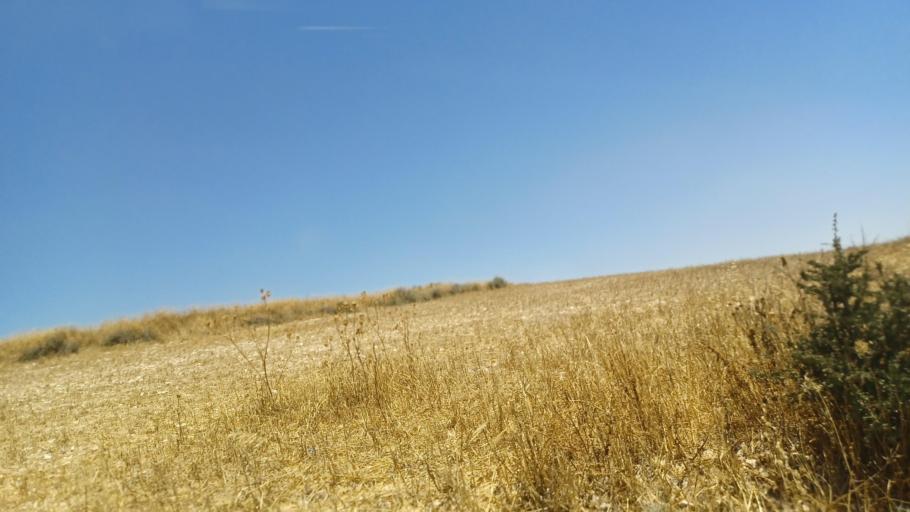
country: CY
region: Lefkosia
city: Lympia
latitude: 34.9919
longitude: 33.4842
